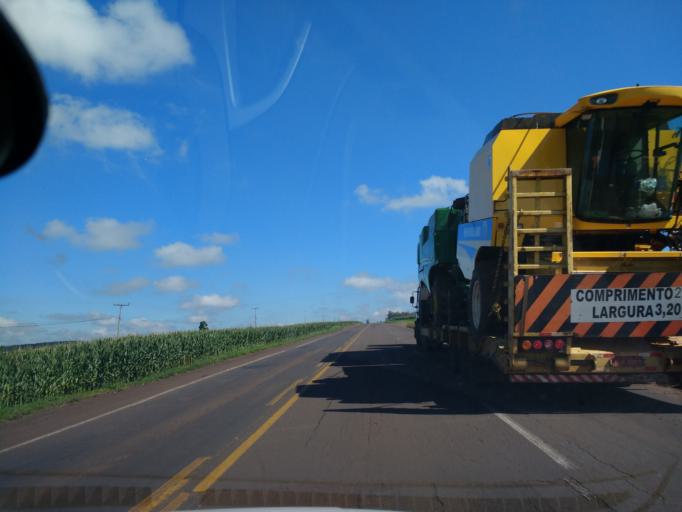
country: BR
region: Parana
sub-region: Cianorte
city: Cianorte
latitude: -23.6543
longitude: -52.5256
